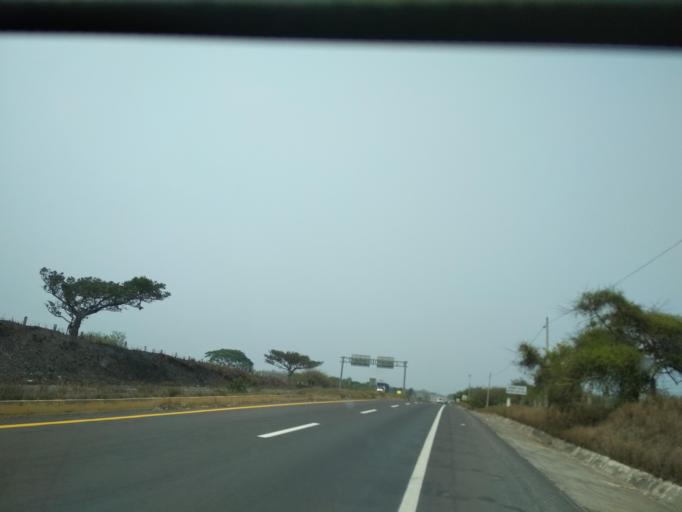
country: MX
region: Veracruz
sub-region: Veracruz
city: Delfino Victoria (Santa Fe)
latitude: 19.1970
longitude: -96.2737
